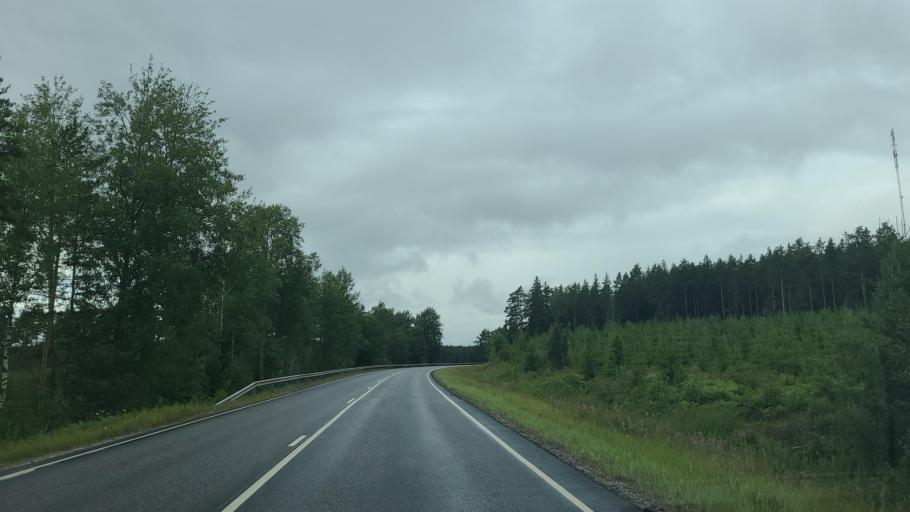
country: FI
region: Varsinais-Suomi
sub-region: Aboland-Turunmaa
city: Kimito
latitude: 60.2036
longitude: 22.6513
